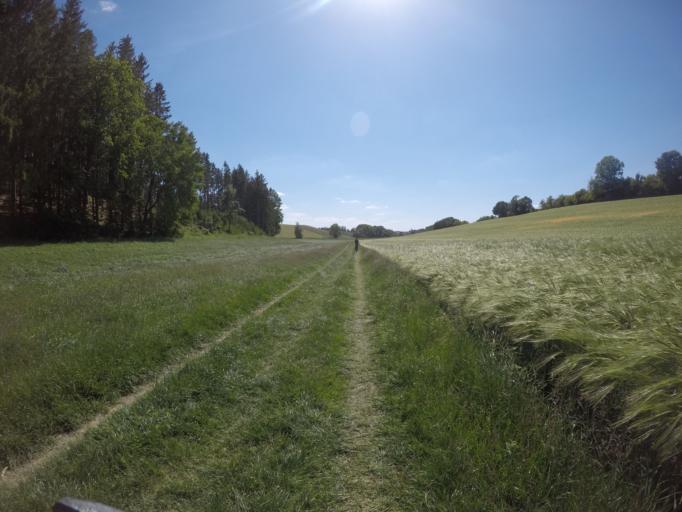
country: DE
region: Bavaria
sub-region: Lower Bavaria
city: Landshut
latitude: 48.5179
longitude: 12.1686
